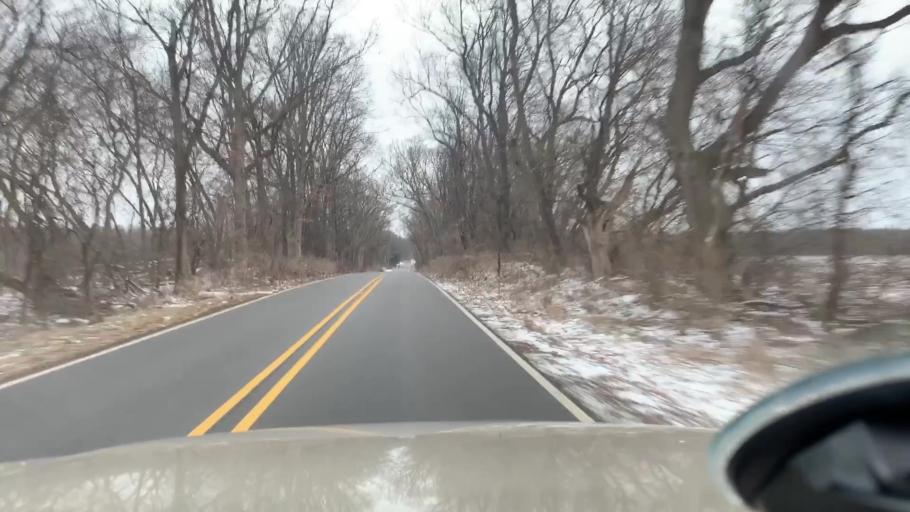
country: US
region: Michigan
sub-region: Jackson County
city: Spring Arbor
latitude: 42.2086
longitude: -84.5309
